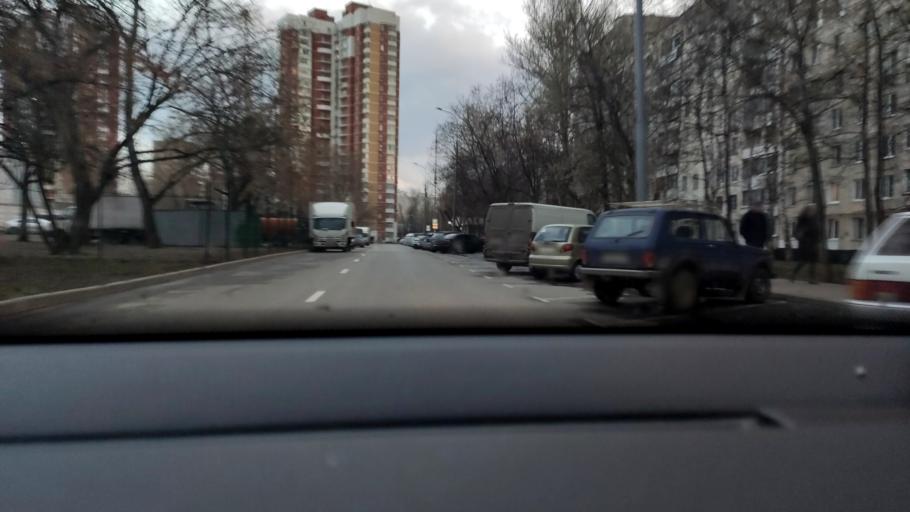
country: RU
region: Moscow
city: Altuf'yevskiy
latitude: 55.8792
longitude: 37.5761
